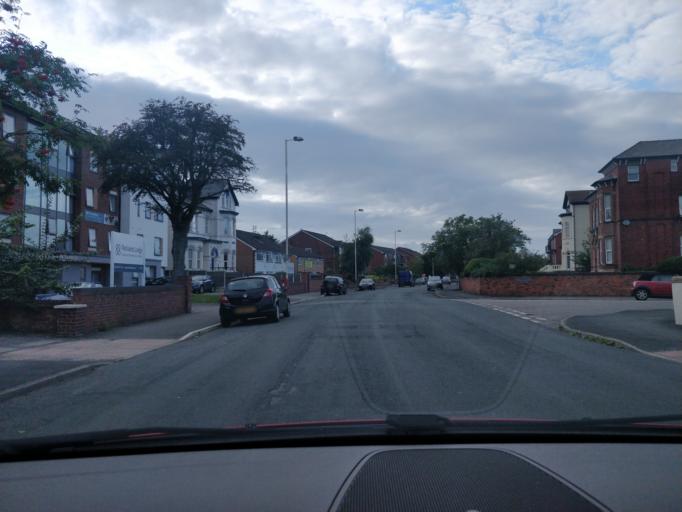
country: GB
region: England
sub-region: Sefton
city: Southport
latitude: 53.6517
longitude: -2.9852
